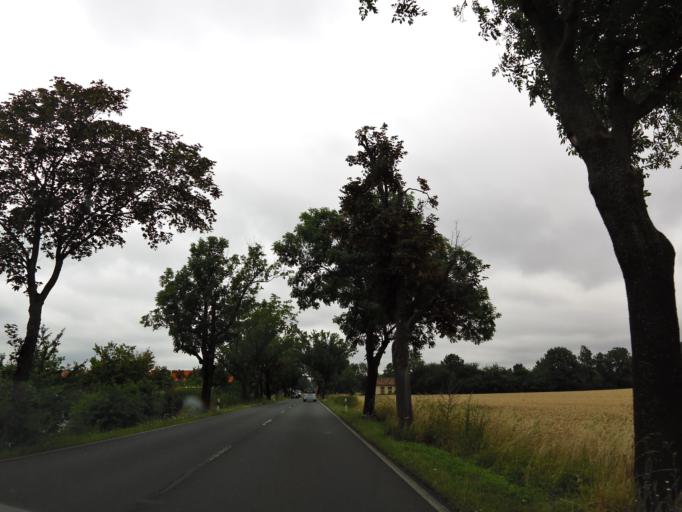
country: DE
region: Saxony
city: Markkleeberg
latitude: 51.2833
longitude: 12.4304
